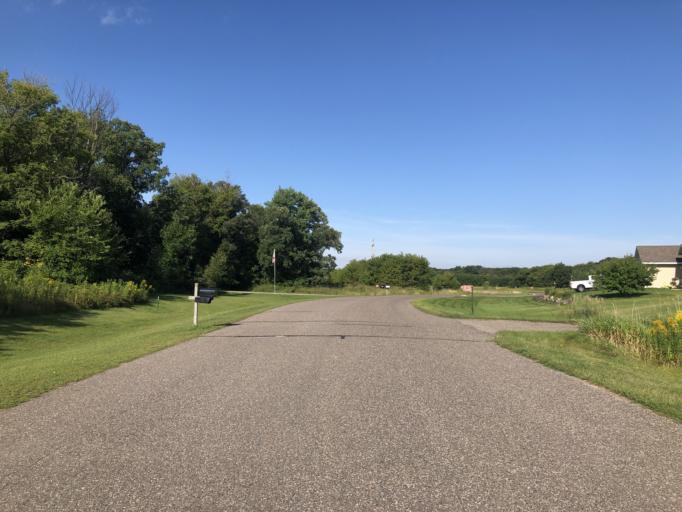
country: US
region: Minnesota
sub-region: Sherburne County
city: Becker
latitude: 45.4236
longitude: -93.8369
